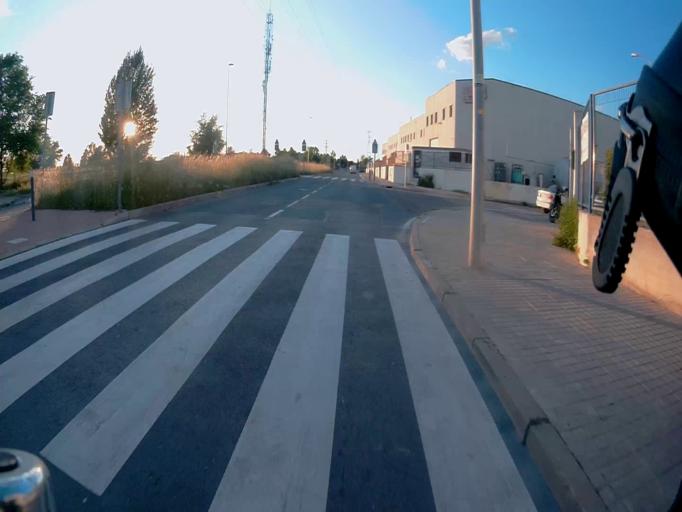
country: ES
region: Madrid
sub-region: Provincia de Madrid
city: Alcorcon
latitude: 40.3346
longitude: -3.8192
